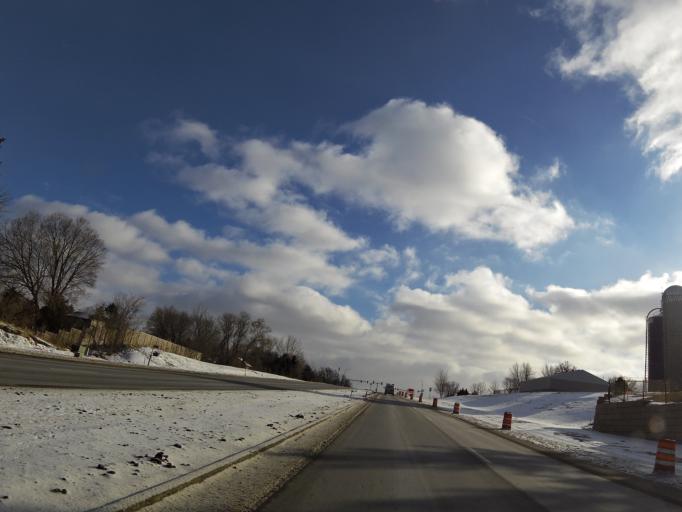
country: US
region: Minnesota
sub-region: Scott County
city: Shakopee
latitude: 44.7641
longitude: -93.5056
